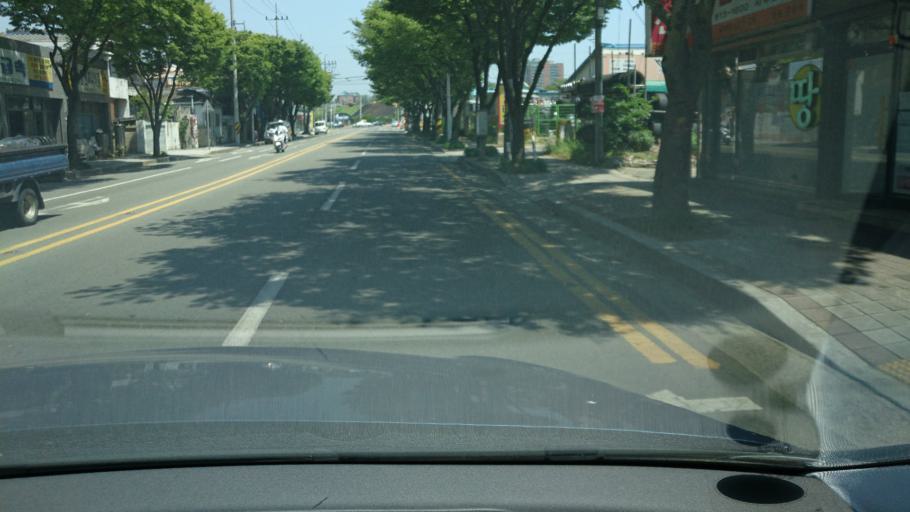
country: KR
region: Gyeongsangbuk-do
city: Gyeongsan-si
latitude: 35.8301
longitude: 128.7390
